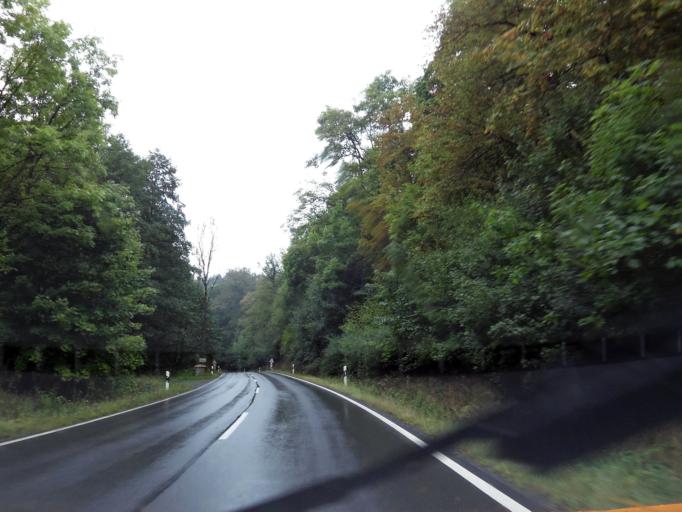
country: DE
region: Saxony-Anhalt
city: Harzgerode
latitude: 51.6764
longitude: 11.1352
